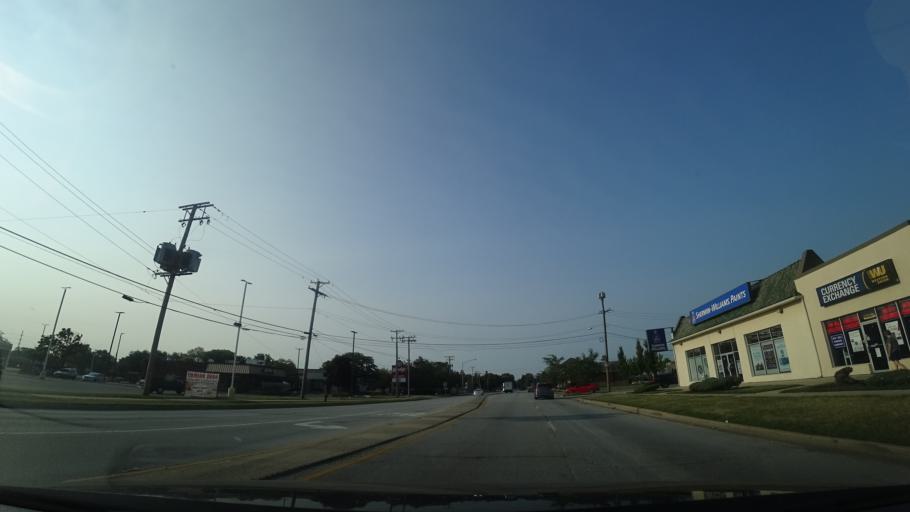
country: US
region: Illinois
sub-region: Cook County
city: Des Plaines
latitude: 42.0252
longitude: -87.8944
